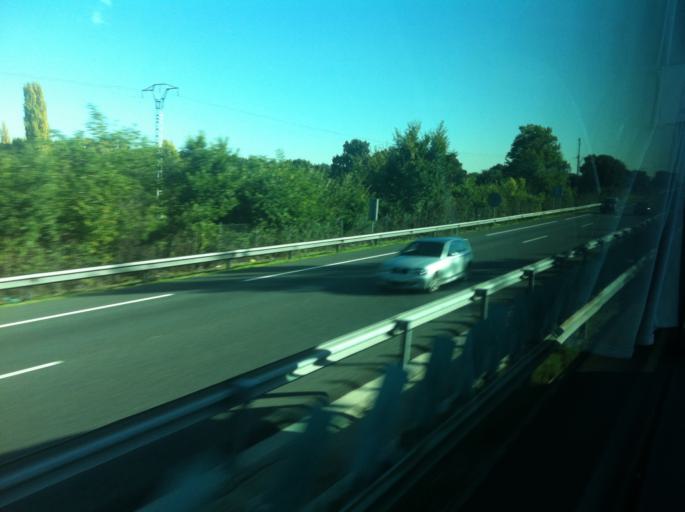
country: ES
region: Madrid
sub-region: Provincia de Madrid
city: San Agustin de Guadalix
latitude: 40.6385
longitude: -3.5923
